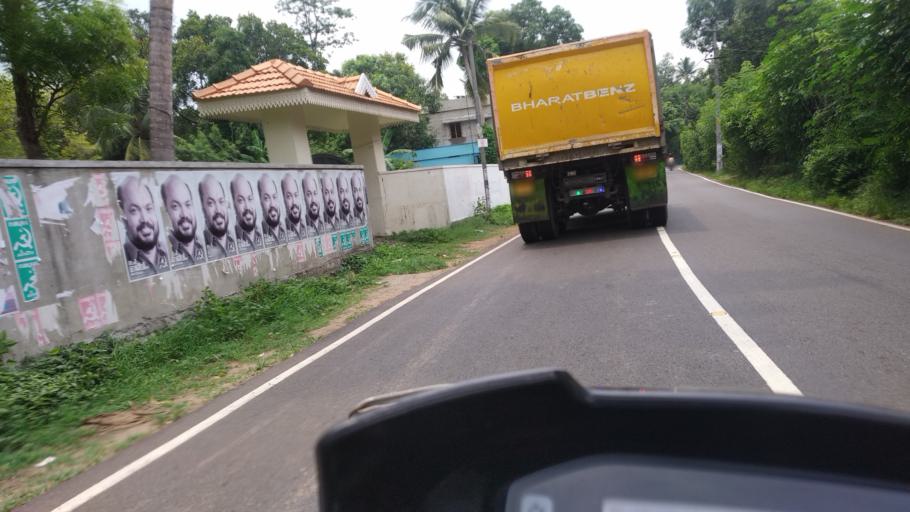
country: IN
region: Kerala
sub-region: Ernakulam
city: Aluva
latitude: 10.1571
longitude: 76.3027
